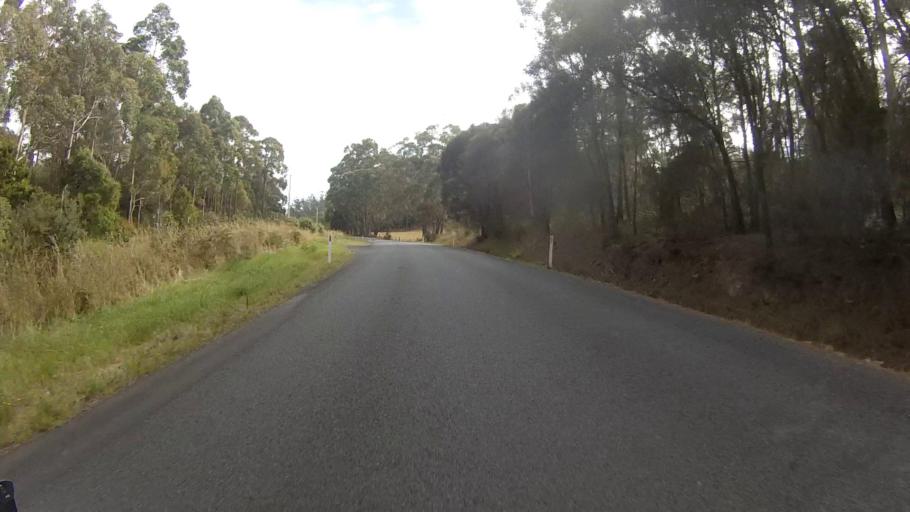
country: AU
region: Tasmania
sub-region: Sorell
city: Sorell
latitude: -42.8112
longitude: 147.7939
